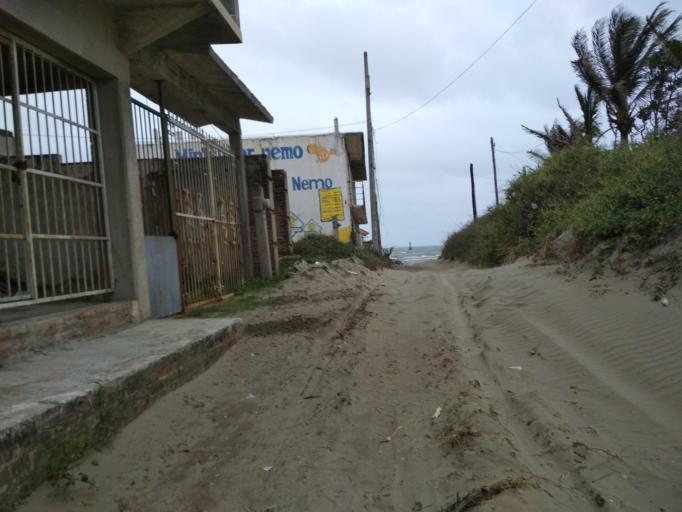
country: MX
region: Veracruz
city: Anton Lizardo
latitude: 19.0601
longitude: -95.9973
